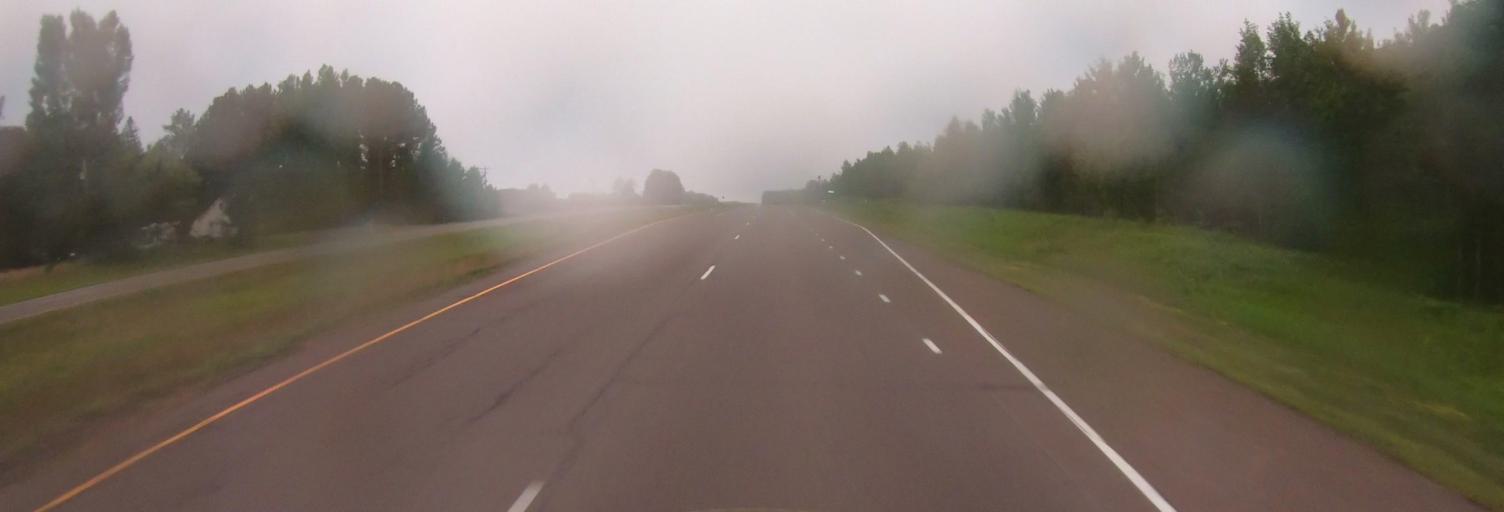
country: US
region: Minnesota
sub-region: Carlton County
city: Cloquet
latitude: 46.9080
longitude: -92.4699
